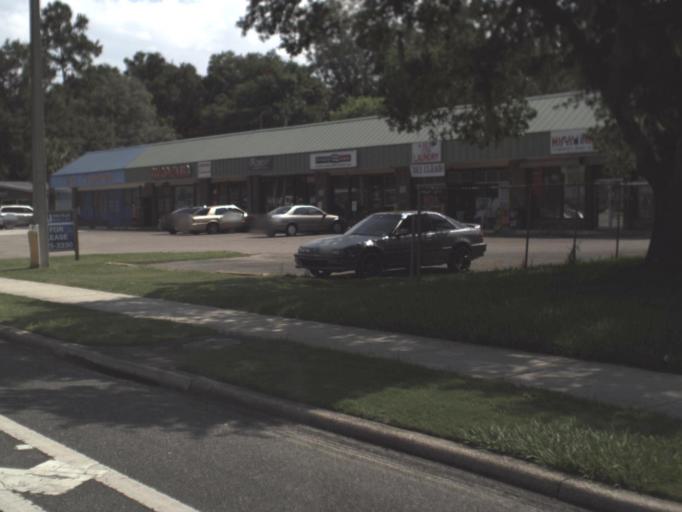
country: US
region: Florida
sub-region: Alachua County
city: Gainesville
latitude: 29.6296
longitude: -82.3393
